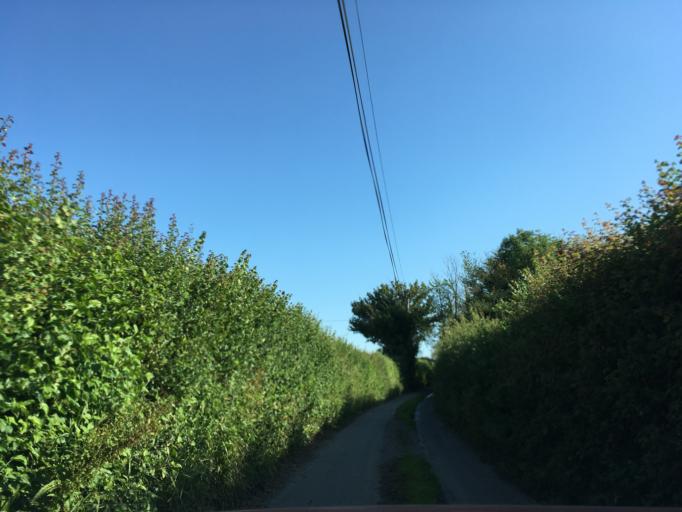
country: GB
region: England
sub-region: South Gloucestershire
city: Siston
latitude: 51.4667
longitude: -2.4374
